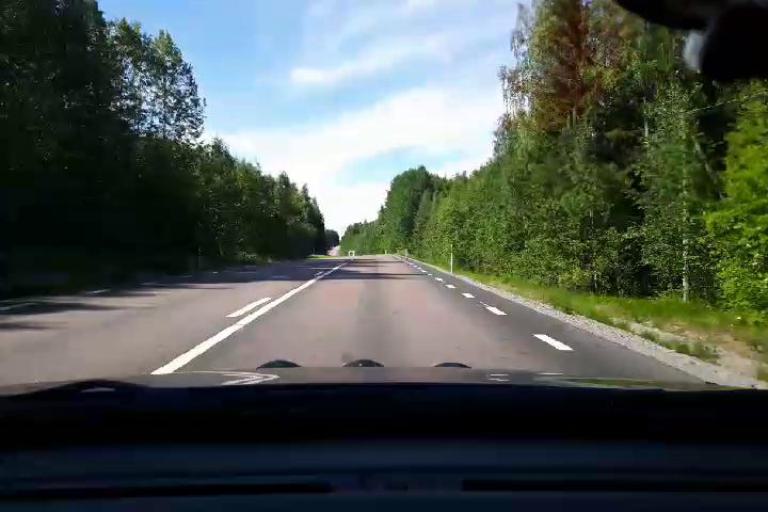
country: SE
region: Gaevleborg
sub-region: Bollnas Kommun
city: Kilafors
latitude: 61.1945
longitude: 16.7670
